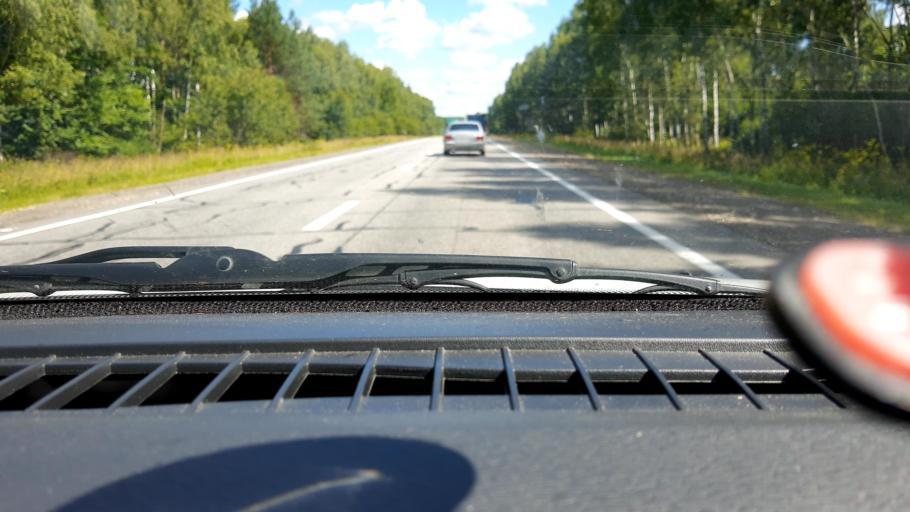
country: RU
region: Nizjnij Novgorod
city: Arzamas
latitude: 55.5384
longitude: 43.9292
